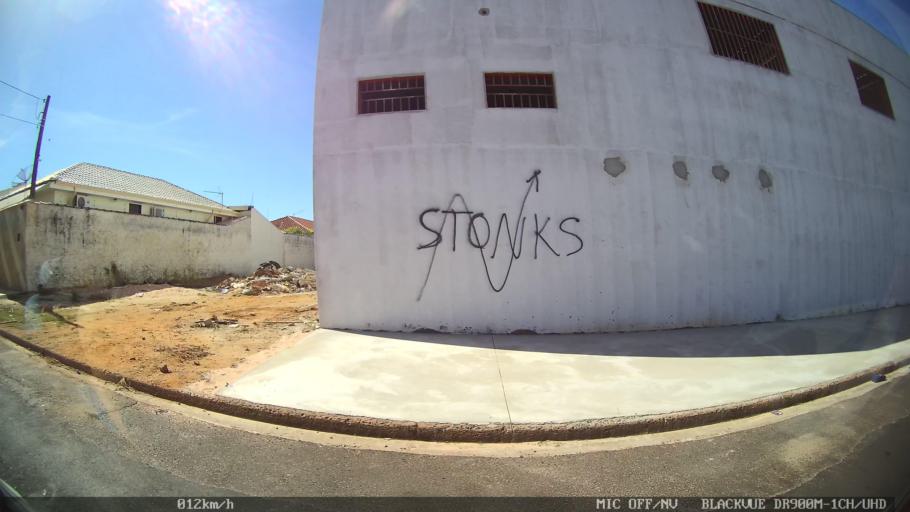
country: BR
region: Sao Paulo
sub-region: Franca
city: Franca
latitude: -20.5437
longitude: -47.3797
